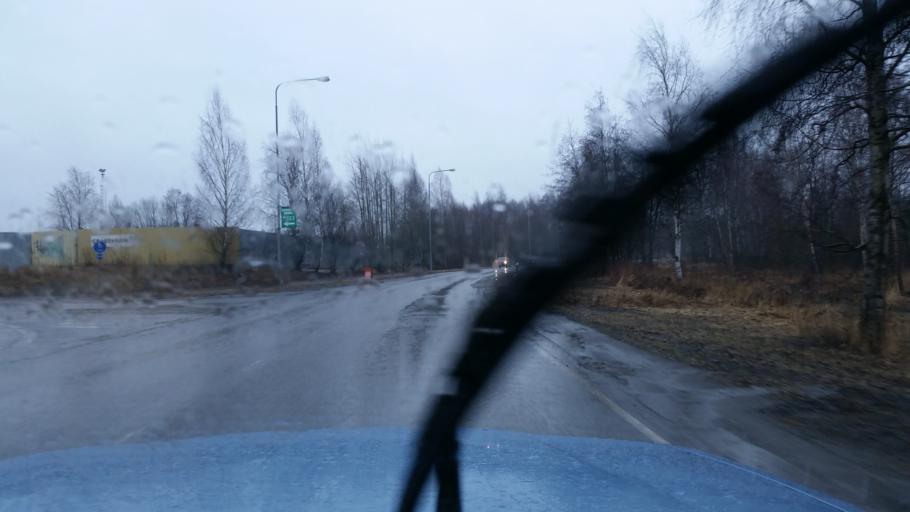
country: FI
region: Pirkanmaa
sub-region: Tampere
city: Tampere
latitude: 61.4749
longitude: 23.7895
